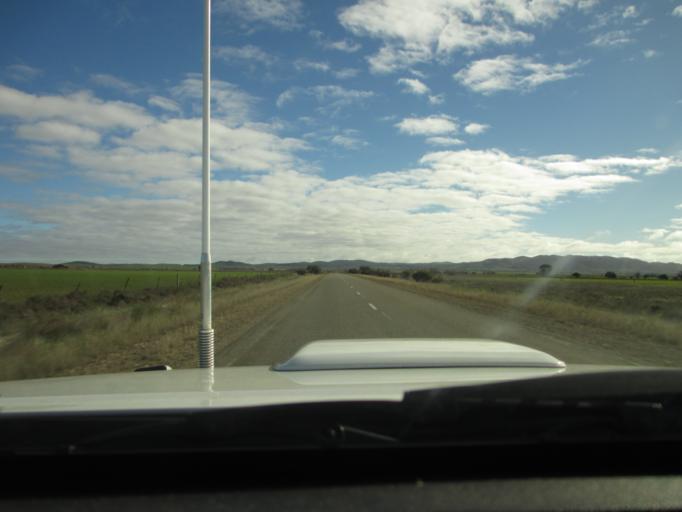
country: AU
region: South Australia
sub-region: Peterborough
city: Peterborough
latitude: -32.6520
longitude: 138.6020
